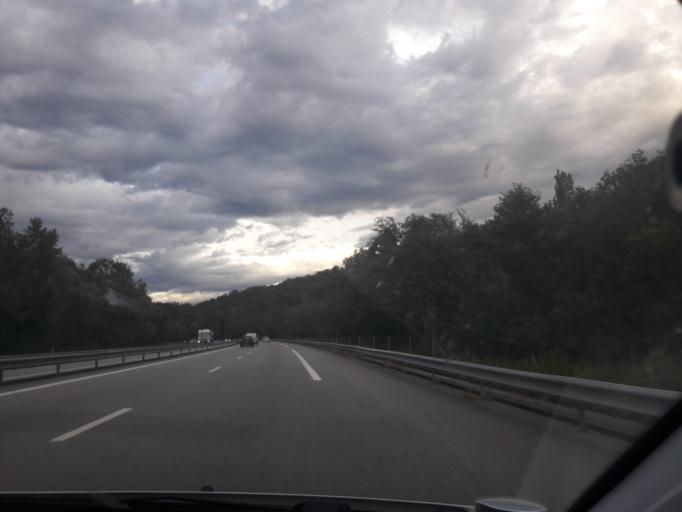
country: FR
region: Rhone-Alpes
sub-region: Departement de la Savoie
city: Cruet
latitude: 45.5082
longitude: 6.0946
